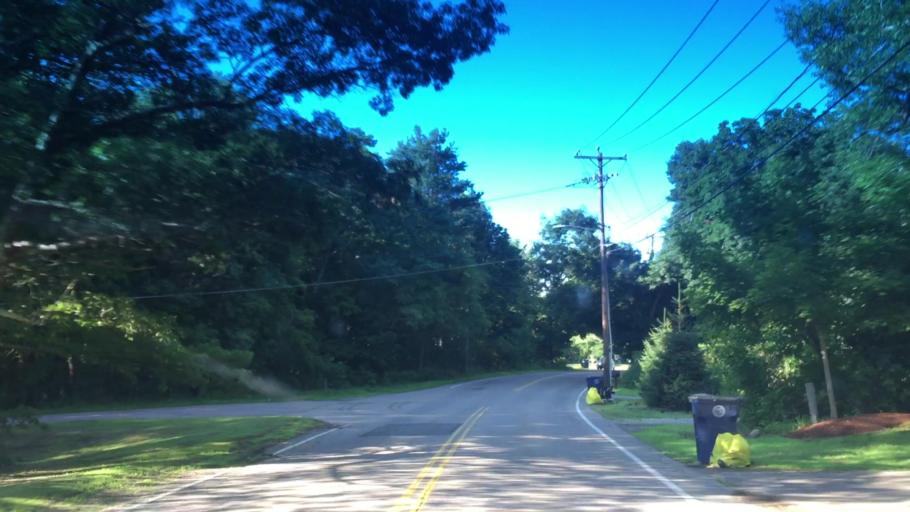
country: US
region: Massachusetts
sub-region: Norfolk County
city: Medway
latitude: 42.1470
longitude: -71.3910
